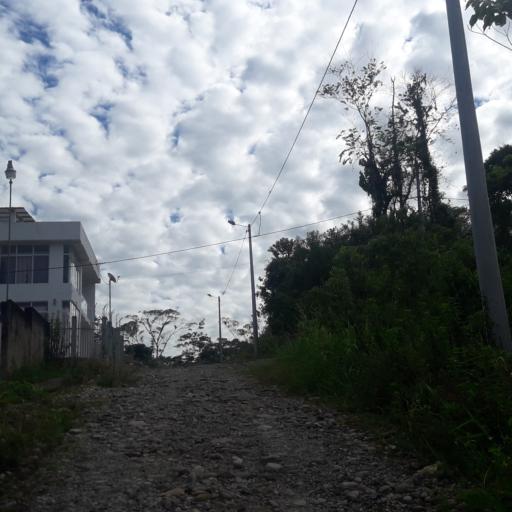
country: EC
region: Napo
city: Tena
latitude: -0.9828
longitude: -77.8261
